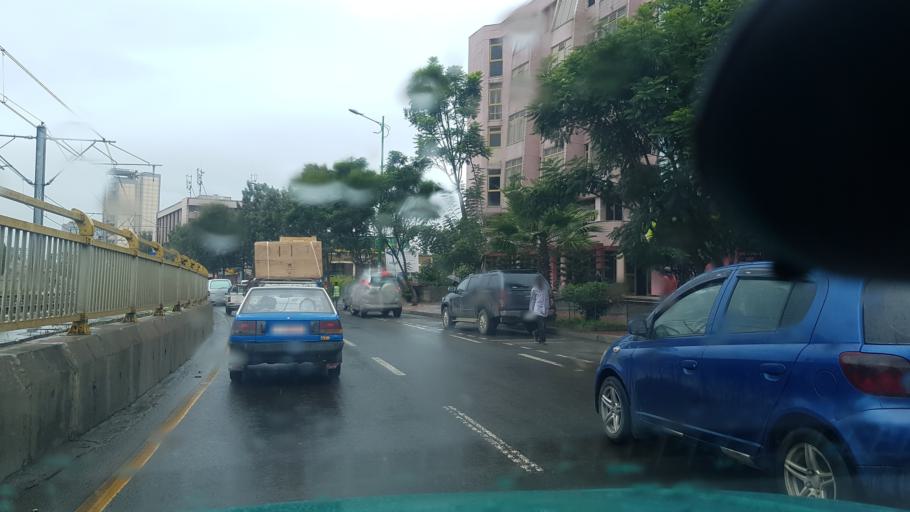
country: ET
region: Adis Abeba
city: Addis Ababa
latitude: 8.9922
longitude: 38.7590
